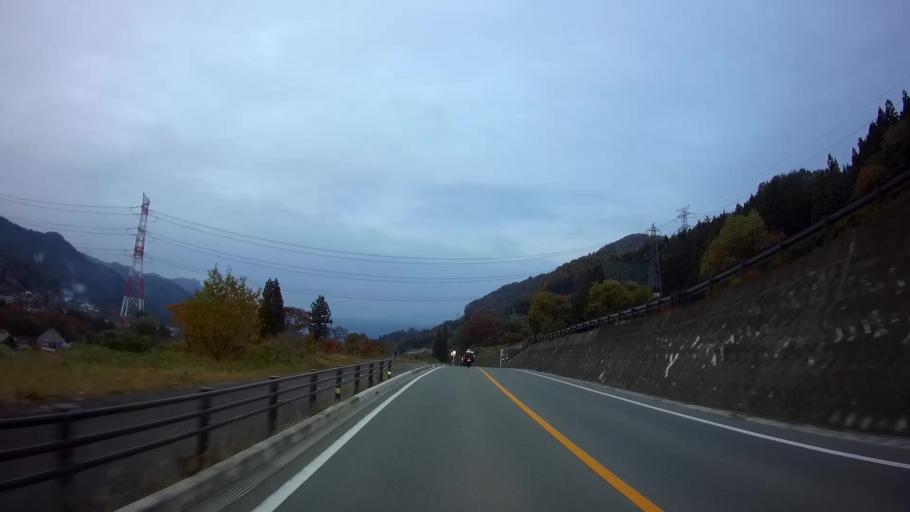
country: JP
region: Gunma
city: Nakanojomachi
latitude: 36.5625
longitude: 138.7511
